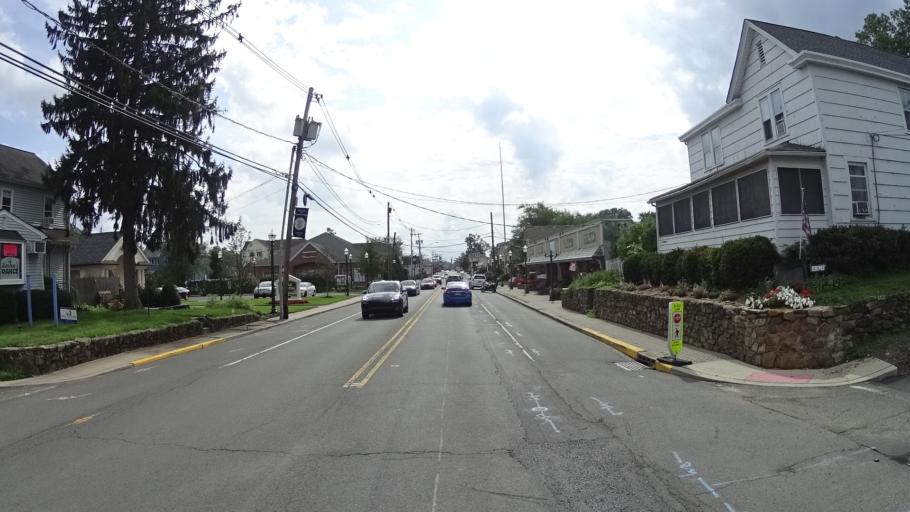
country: US
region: New Jersey
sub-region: Union County
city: Berkeley Heights
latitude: 40.6842
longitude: -74.4409
